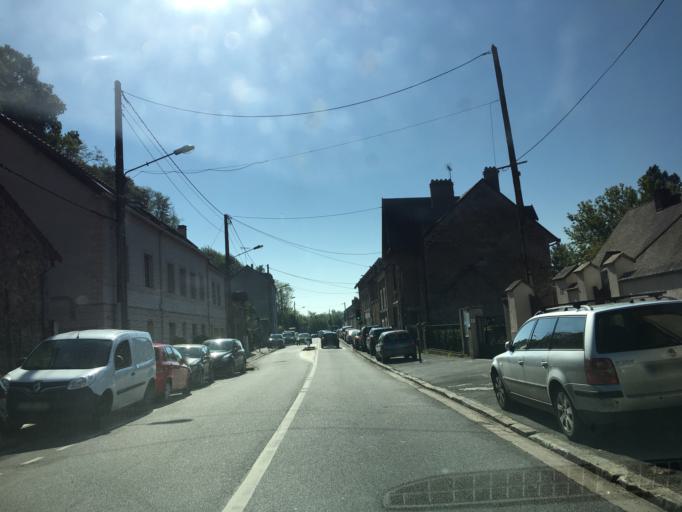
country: FR
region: Ile-de-France
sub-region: Departement des Yvelines
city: Les Loges-en-Josas
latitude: 48.7700
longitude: 2.1484
